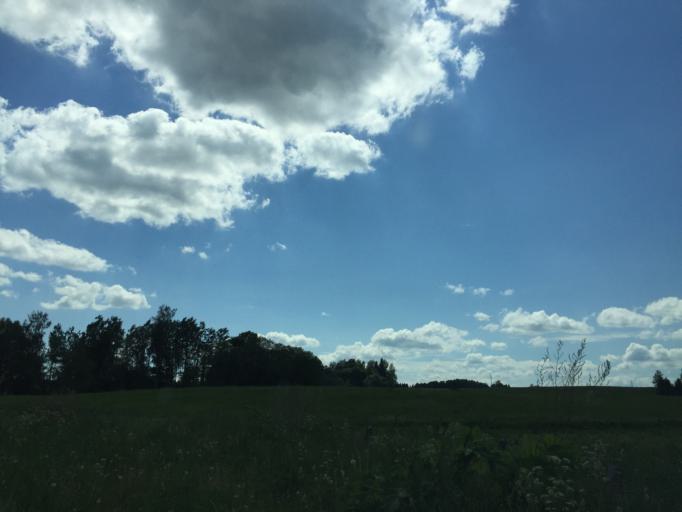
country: LV
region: Priekuli
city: Priekuli
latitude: 57.2260
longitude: 25.4338
